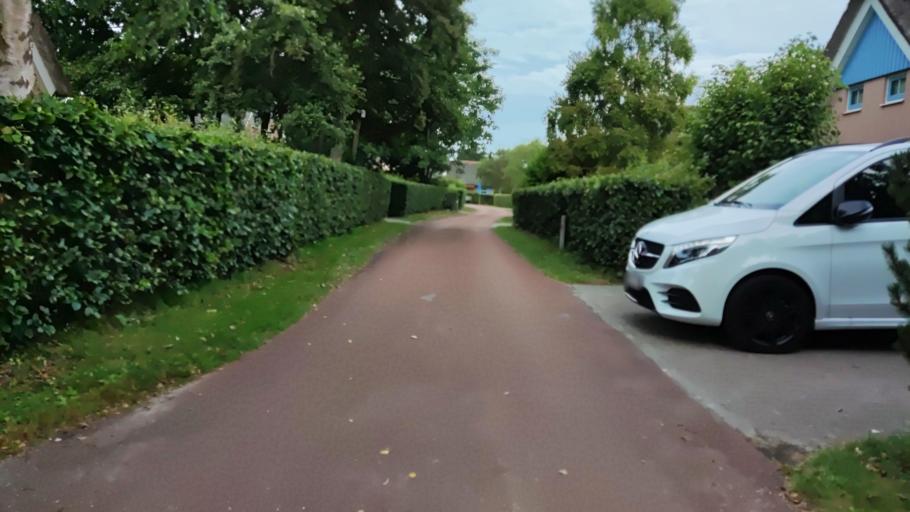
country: NL
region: North Holland
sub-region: Gemeente Texel
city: Den Burg
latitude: 53.0883
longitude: 4.7687
